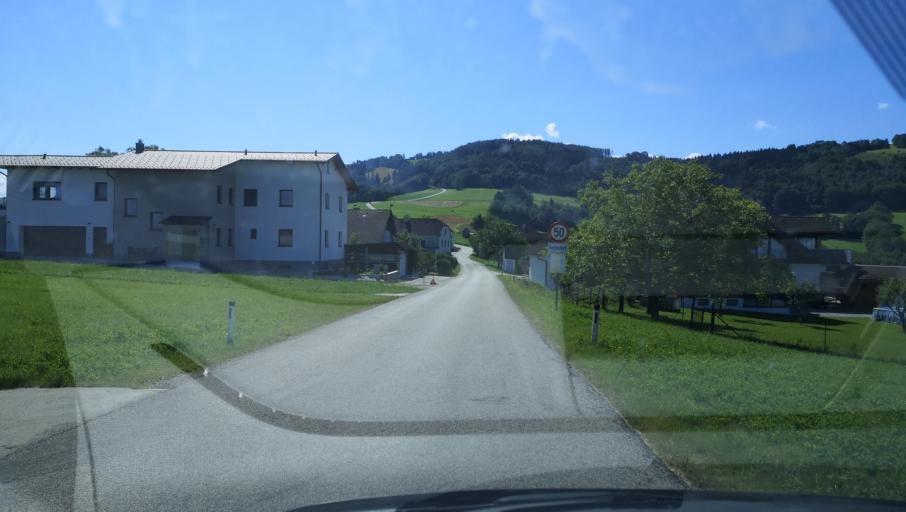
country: AT
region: Lower Austria
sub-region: Politischer Bezirk Amstetten
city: Euratsfeld
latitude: 48.0453
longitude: 14.9199
